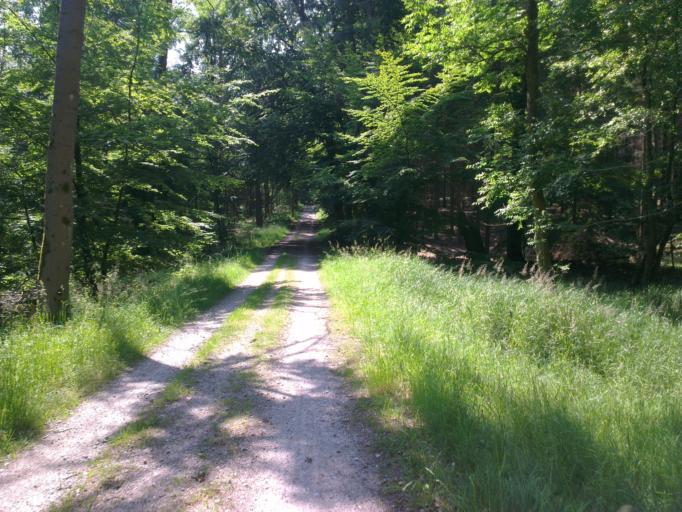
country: DK
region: Capital Region
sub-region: Allerod Kommune
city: Lillerod
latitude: 55.9173
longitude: 12.3595
